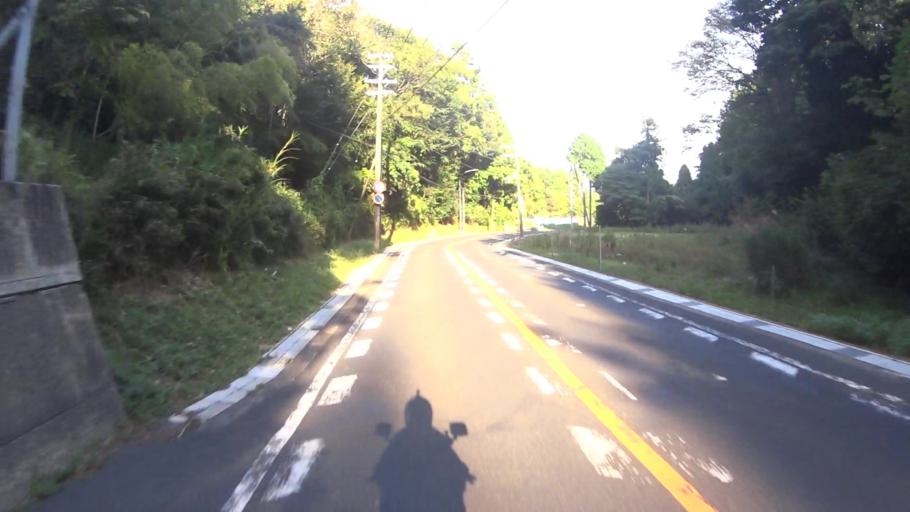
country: JP
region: Hyogo
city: Toyooka
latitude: 35.5929
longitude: 134.9144
